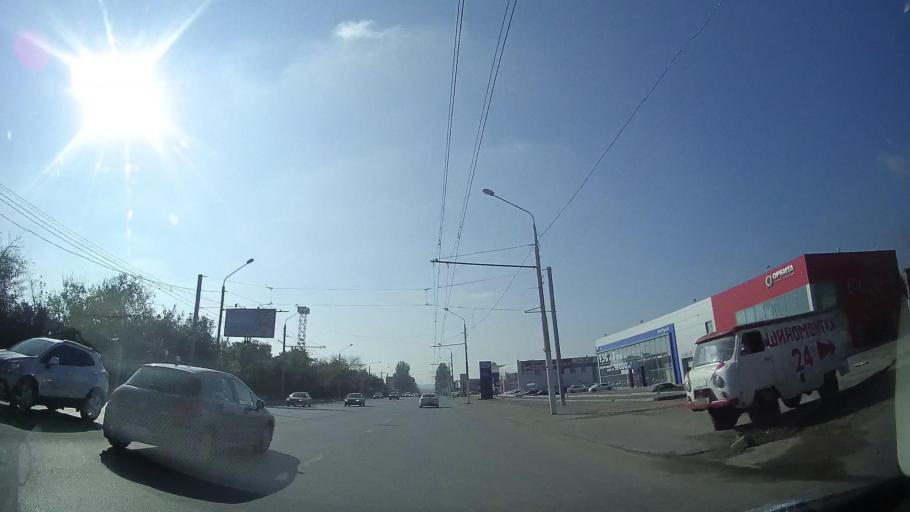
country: RU
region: Rostov
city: Severnyy
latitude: 47.2711
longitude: 39.6850
